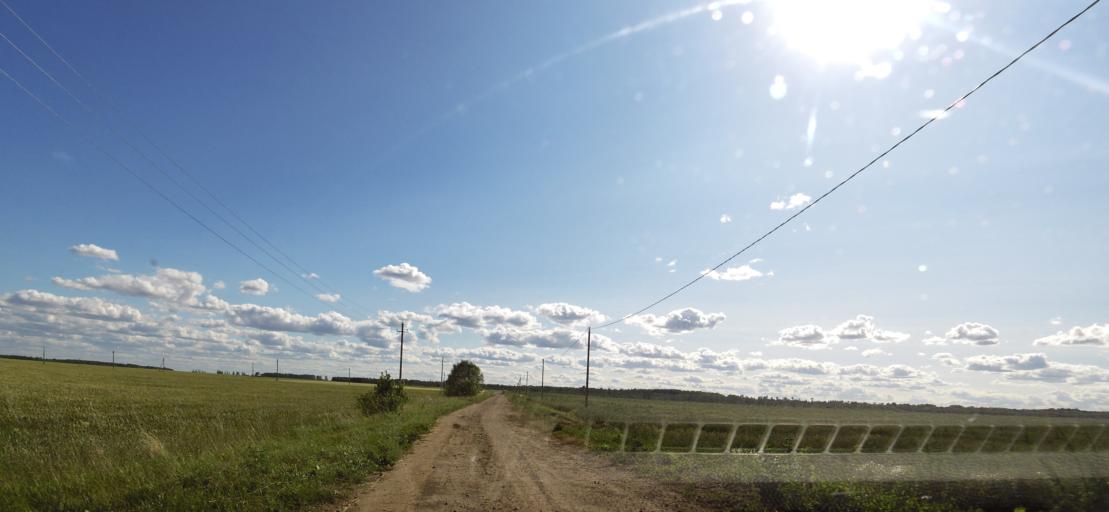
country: LT
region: Panevezys
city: Pasvalys
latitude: 56.1702
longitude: 24.4288
